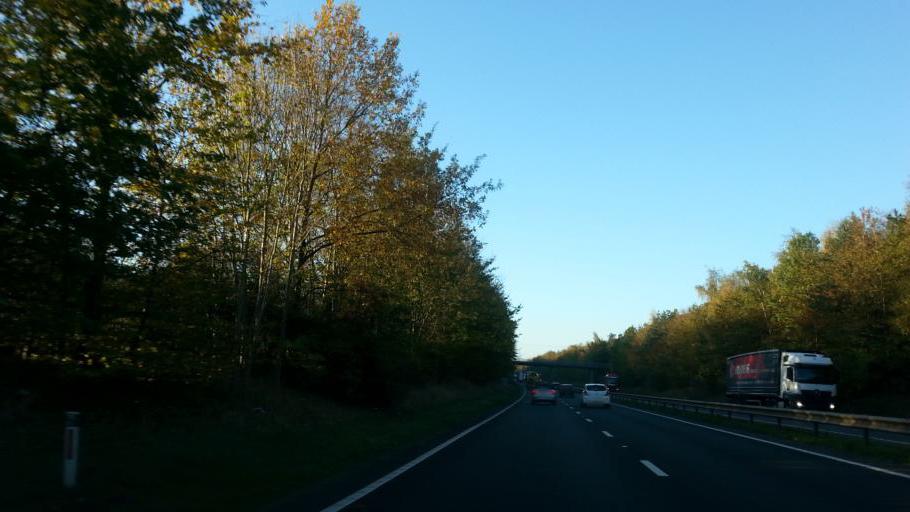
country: GB
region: England
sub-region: Derbyshire
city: Melbourne
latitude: 52.7841
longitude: -1.4135
